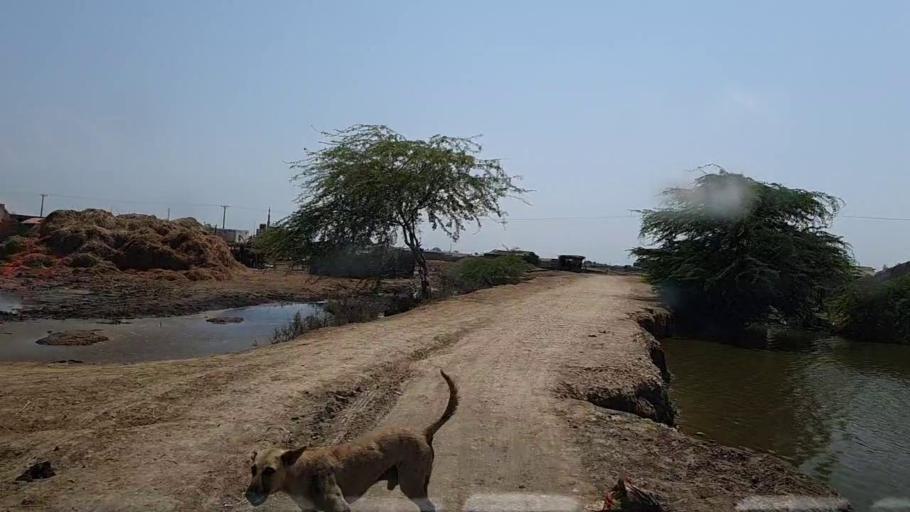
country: PK
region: Sindh
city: Kario
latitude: 24.6369
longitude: 68.4905
